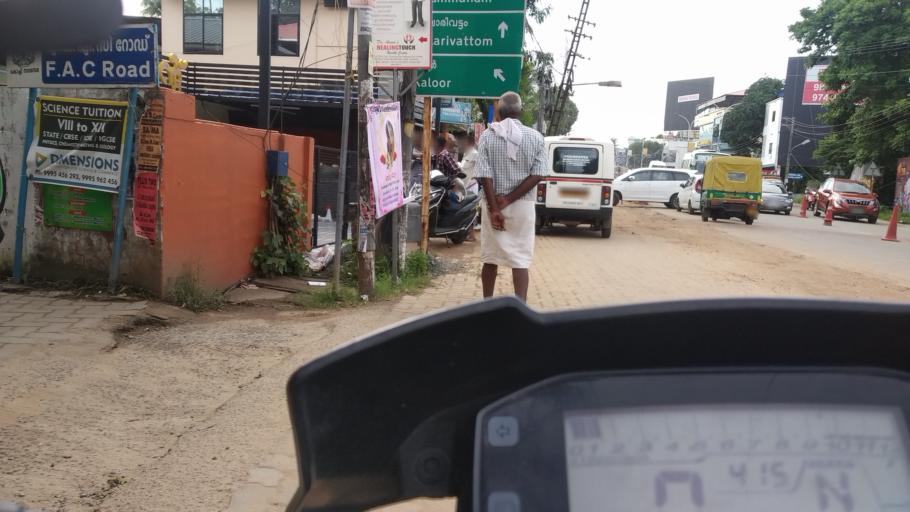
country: IN
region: Kerala
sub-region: Ernakulam
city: Cochin
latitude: 9.9727
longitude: 76.3165
